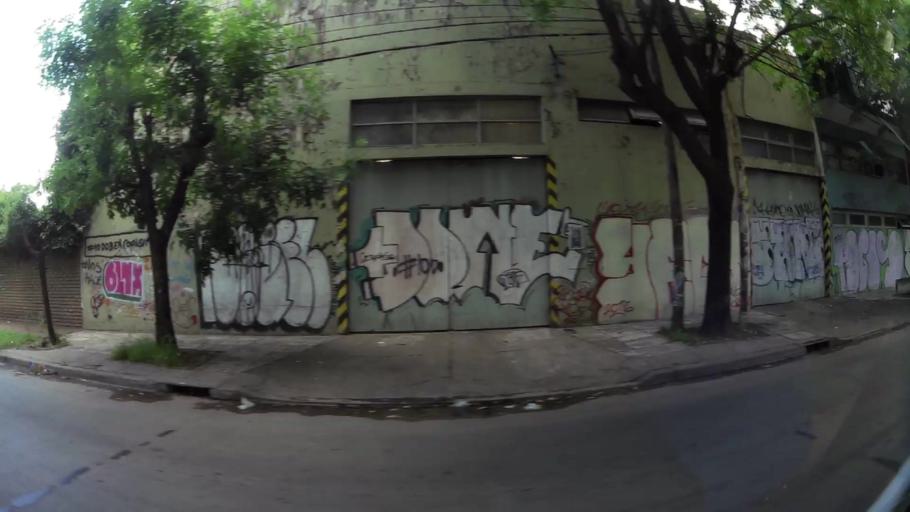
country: AR
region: Buenos Aires
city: San Justo
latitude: -34.6622
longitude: -58.5611
